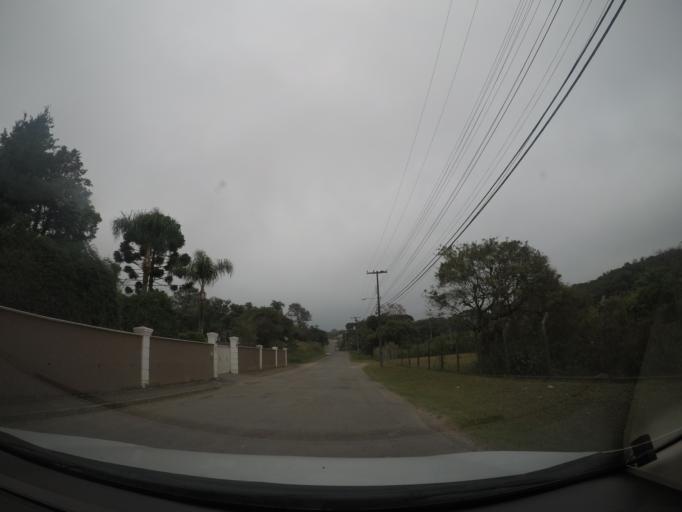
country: BR
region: Parana
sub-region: Colombo
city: Colombo
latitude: -25.3378
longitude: -49.2536
